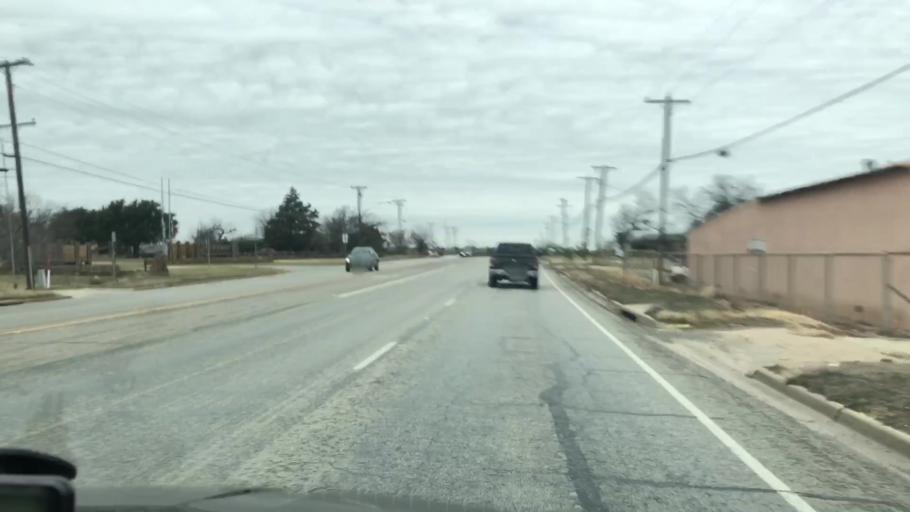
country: US
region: Texas
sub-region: Jack County
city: Jacksboro
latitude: 33.2068
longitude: -98.1546
